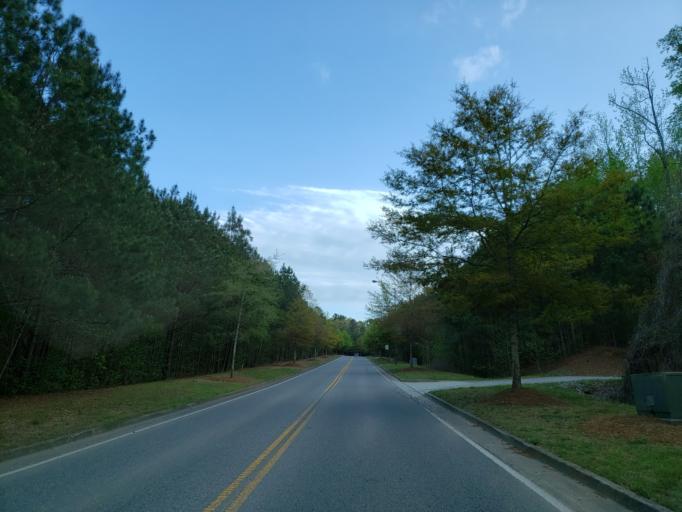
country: US
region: Georgia
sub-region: Cherokee County
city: Canton
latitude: 34.2916
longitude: -84.4634
